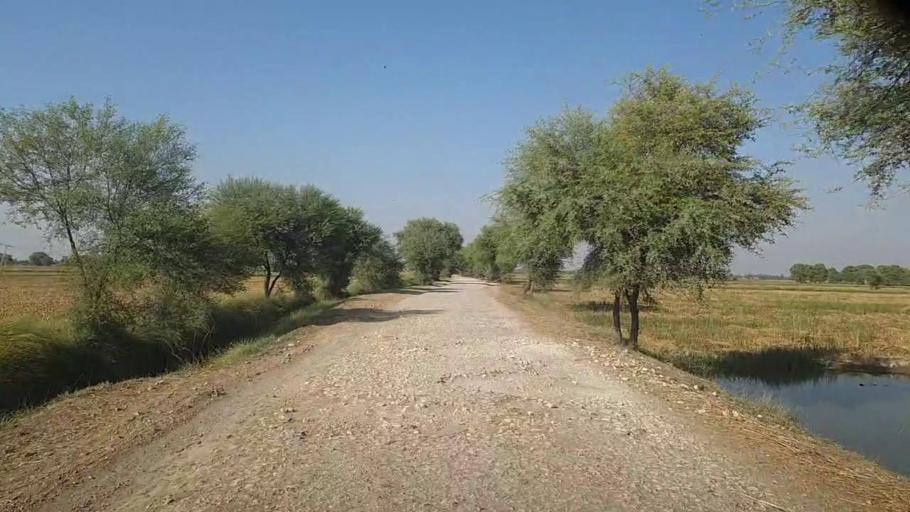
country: PK
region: Sindh
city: Tangwani
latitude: 28.2829
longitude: 68.9844
